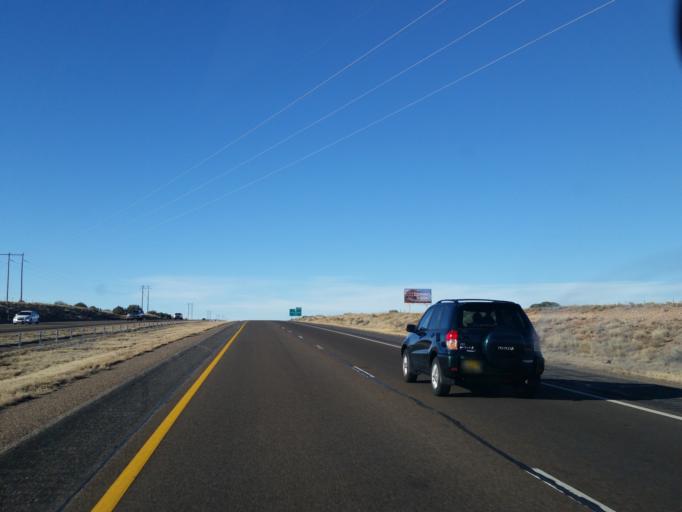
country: US
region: New Mexico
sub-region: Sandoval County
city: Santo Domingo Pueblo
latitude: 35.4804
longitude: -106.2800
